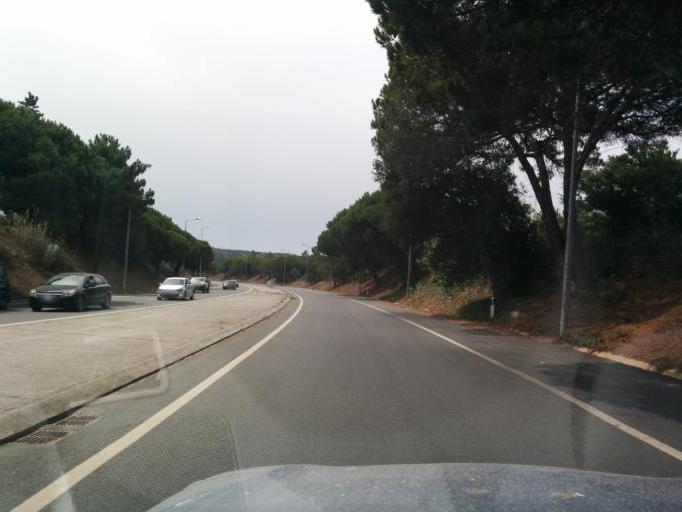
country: PT
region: Beja
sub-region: Odemira
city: Vila Nova de Milfontes
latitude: 37.7319
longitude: -8.7719
